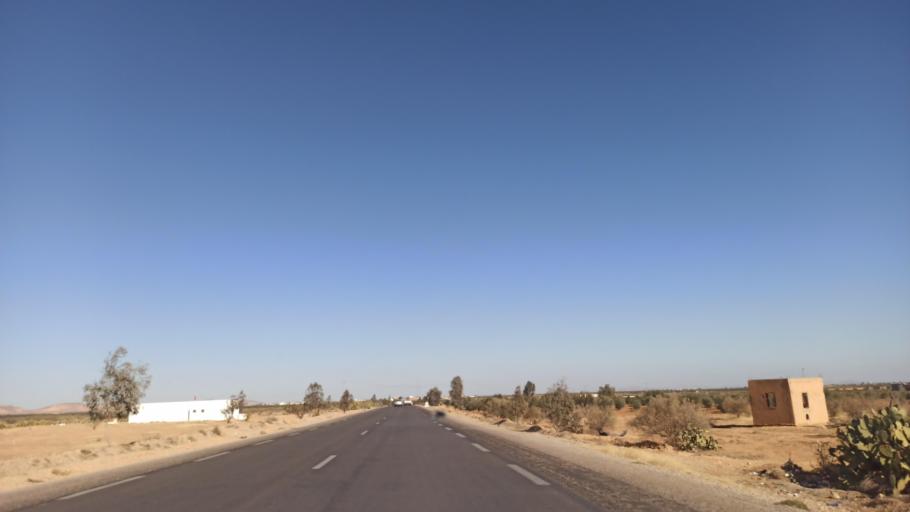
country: TN
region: Sidi Bu Zayd
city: Bi'r al Hufayy
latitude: 34.9557
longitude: 9.2164
